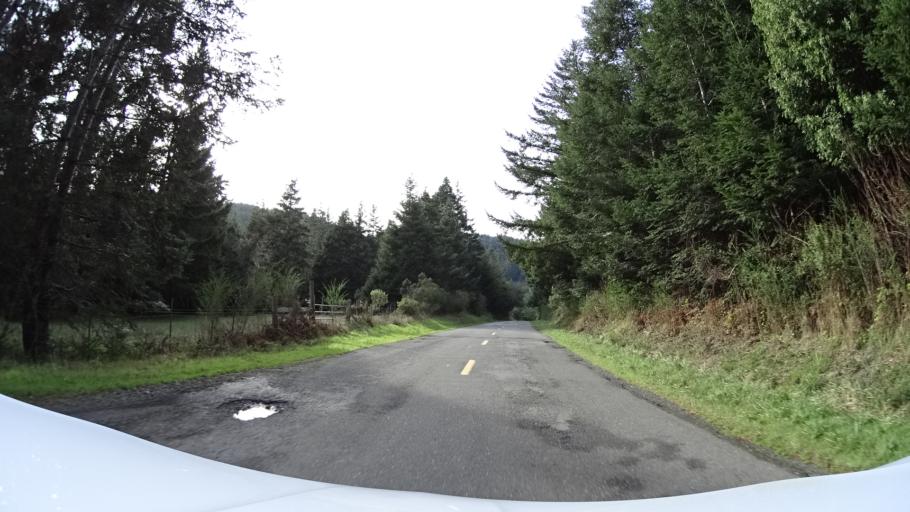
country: US
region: California
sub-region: Humboldt County
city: Ferndale
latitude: 40.3469
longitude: -124.3357
